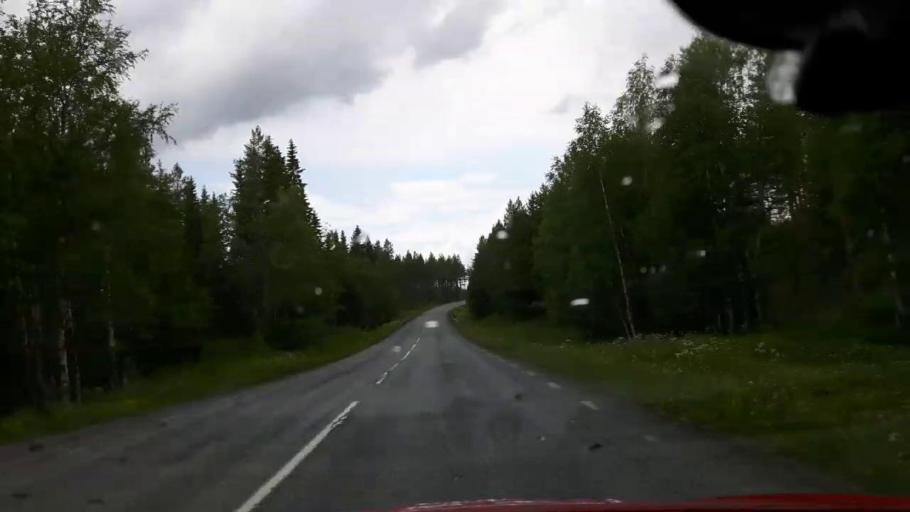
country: SE
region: Jaemtland
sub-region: Krokoms Kommun
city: Krokom
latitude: 63.4076
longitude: 14.2537
